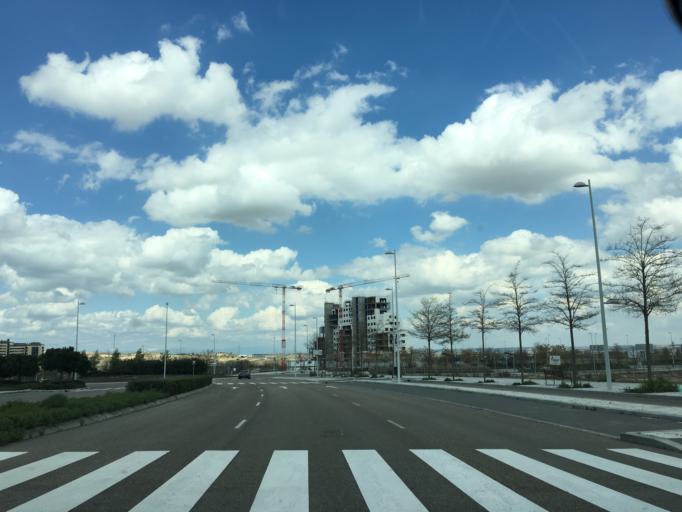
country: ES
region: Madrid
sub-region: Provincia de Madrid
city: Hortaleza
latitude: 40.4899
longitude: -3.6107
